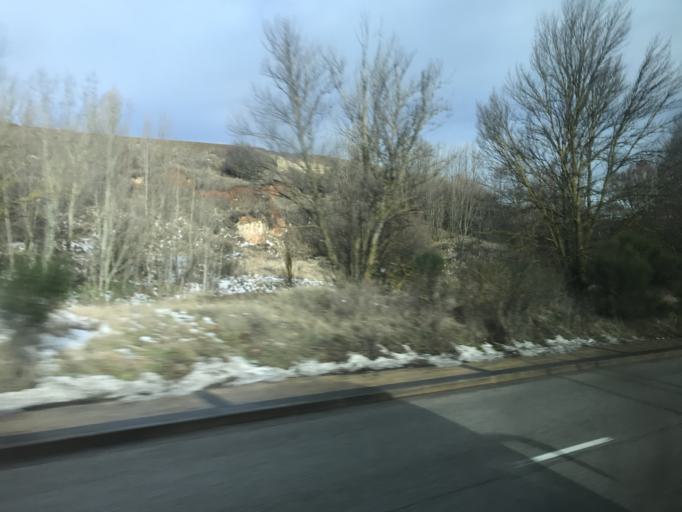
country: ES
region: Castille and Leon
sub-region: Provincia de Burgos
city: Burgos
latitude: 42.3262
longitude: -3.7011
